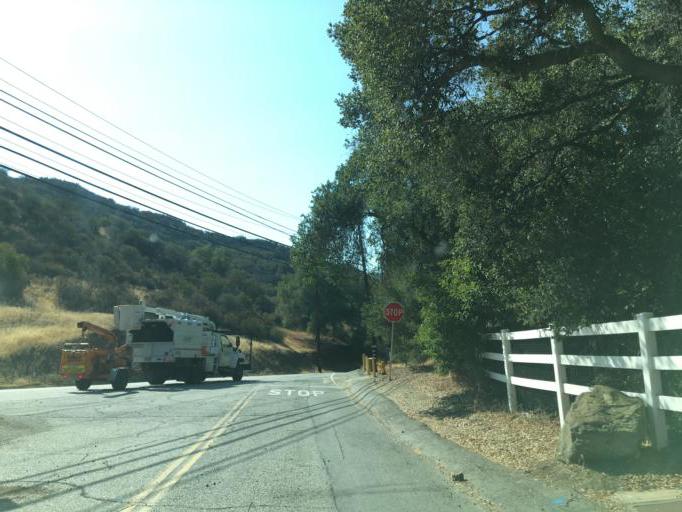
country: US
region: California
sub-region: Los Angeles County
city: Hidden Hills
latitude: 34.1062
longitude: -118.6613
